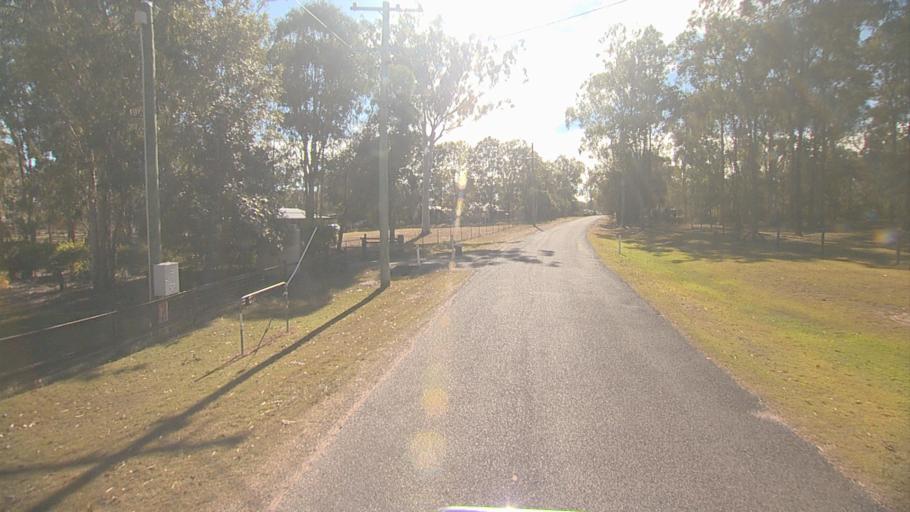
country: AU
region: Queensland
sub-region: Logan
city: Chambers Flat
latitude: -27.7907
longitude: 153.0659
